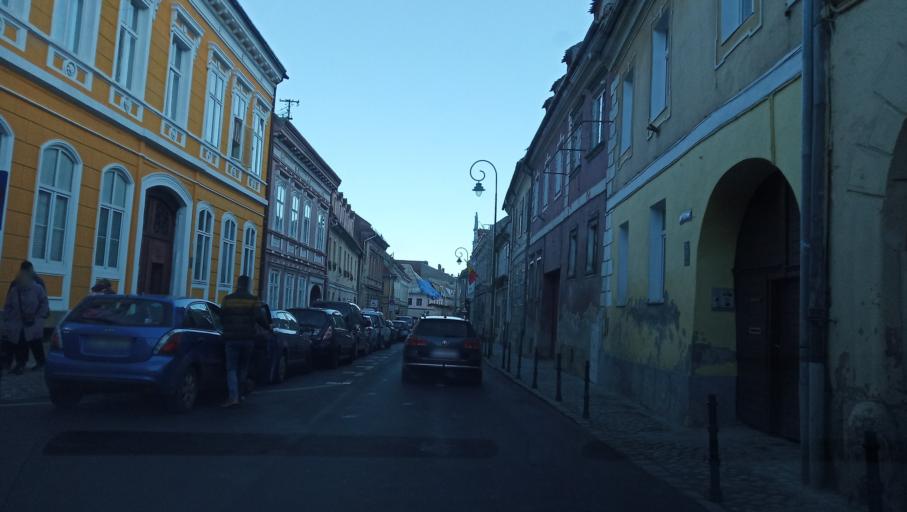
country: RO
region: Brasov
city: Brasov
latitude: 45.6399
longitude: 25.5882
